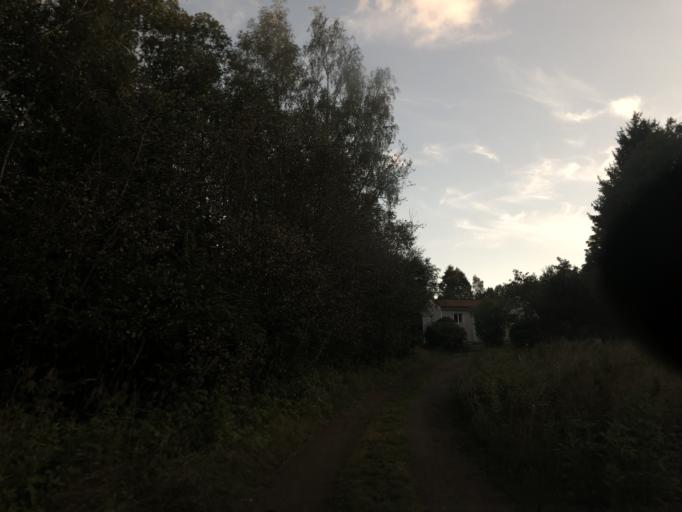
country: SE
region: Vaestra Goetaland
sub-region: Goteborg
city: Majorna
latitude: 57.7622
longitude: 11.9112
